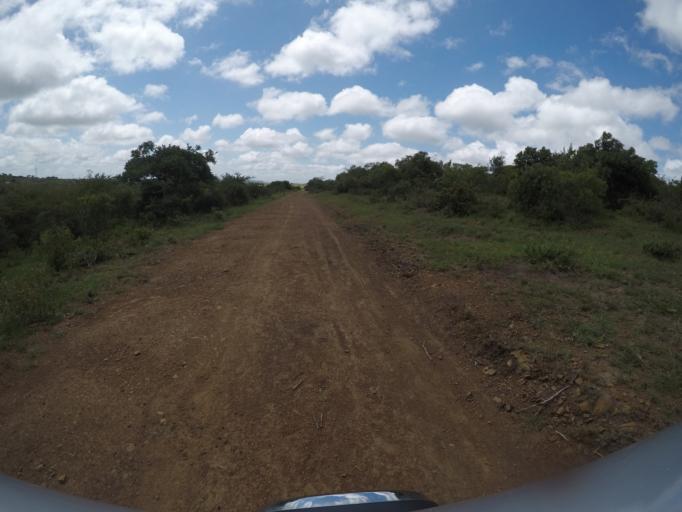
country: ZA
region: KwaZulu-Natal
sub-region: uThungulu District Municipality
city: Empangeni
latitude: -28.5845
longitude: 31.8299
